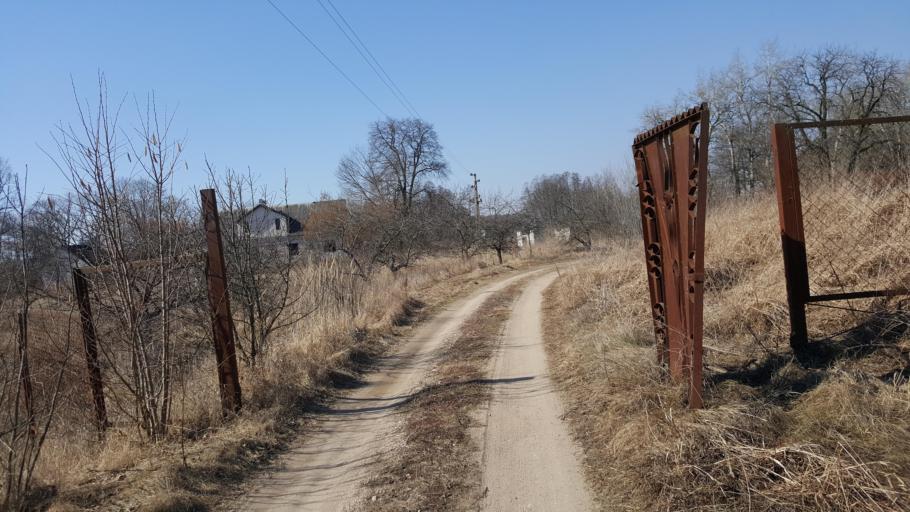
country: BY
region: Brest
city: Kamyanyets
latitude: 52.3624
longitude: 23.7450
